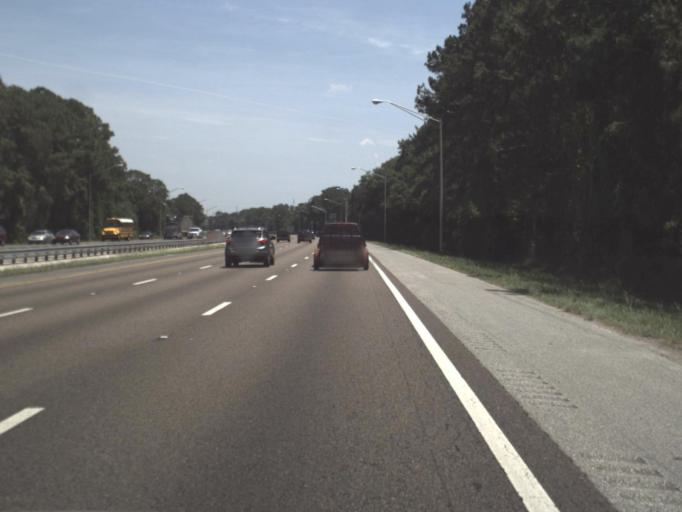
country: US
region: Florida
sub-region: Saint Johns County
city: Fruit Cove
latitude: 30.1748
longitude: -81.6187
